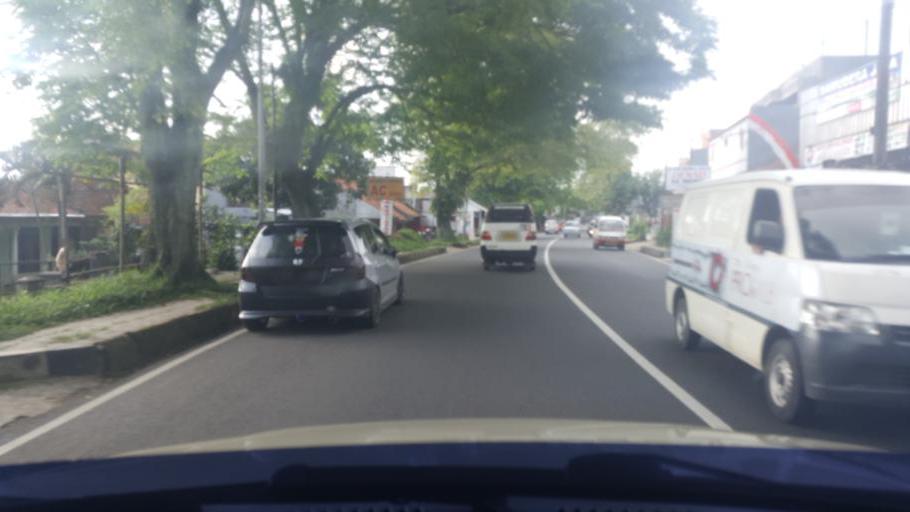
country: ID
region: West Java
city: Mancogeh
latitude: -7.3135
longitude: 108.2123
